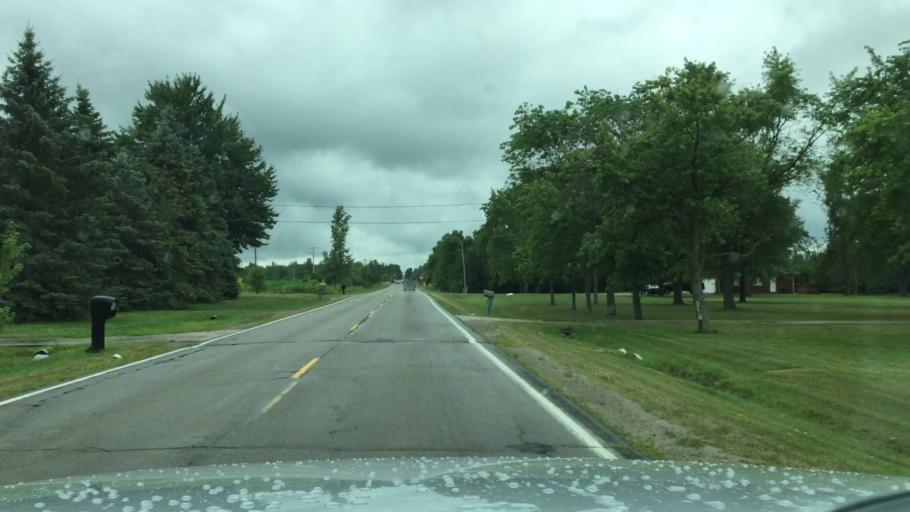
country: US
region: Michigan
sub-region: Genesee County
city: Clio
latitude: 43.1239
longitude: -83.7738
